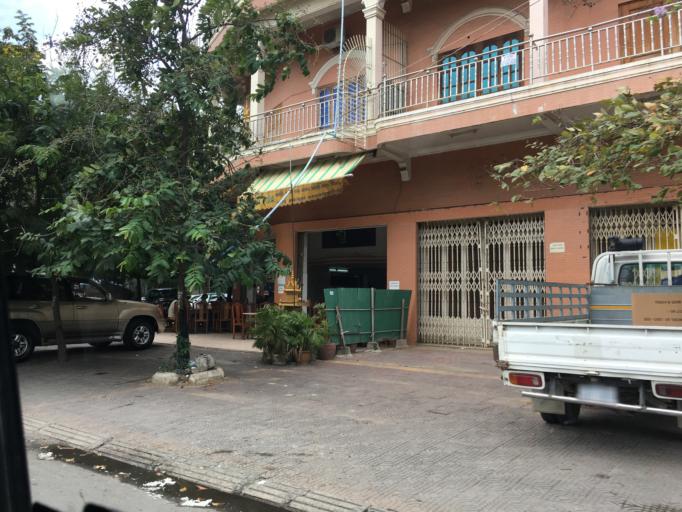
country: KH
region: Phnom Penh
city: Phnom Penh
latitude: 11.5379
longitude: 104.9234
